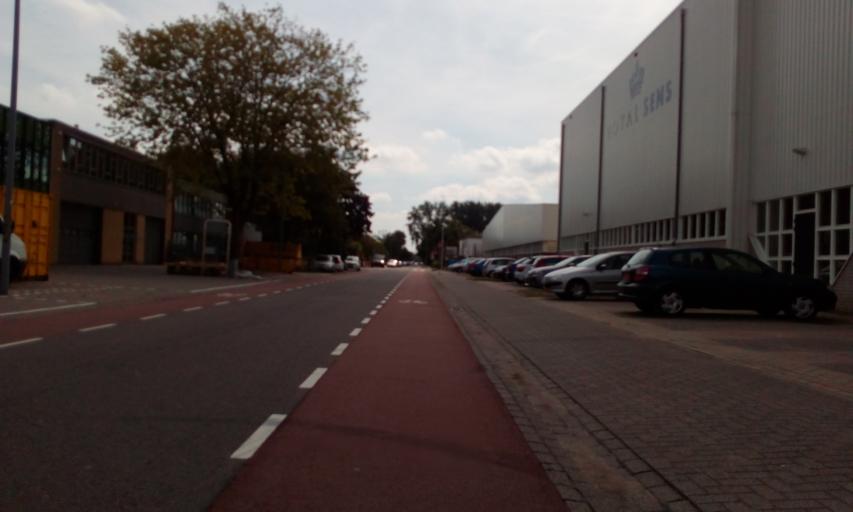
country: NL
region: South Holland
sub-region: Gemeente Lansingerland
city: Berkel en Rodenrijs
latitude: 51.9667
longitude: 4.4646
